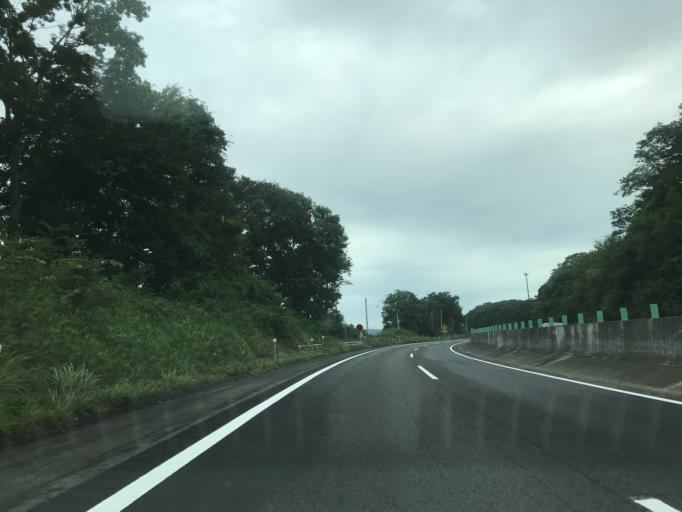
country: JP
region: Miyagi
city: Sendai-shi
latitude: 38.3035
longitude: 140.8096
